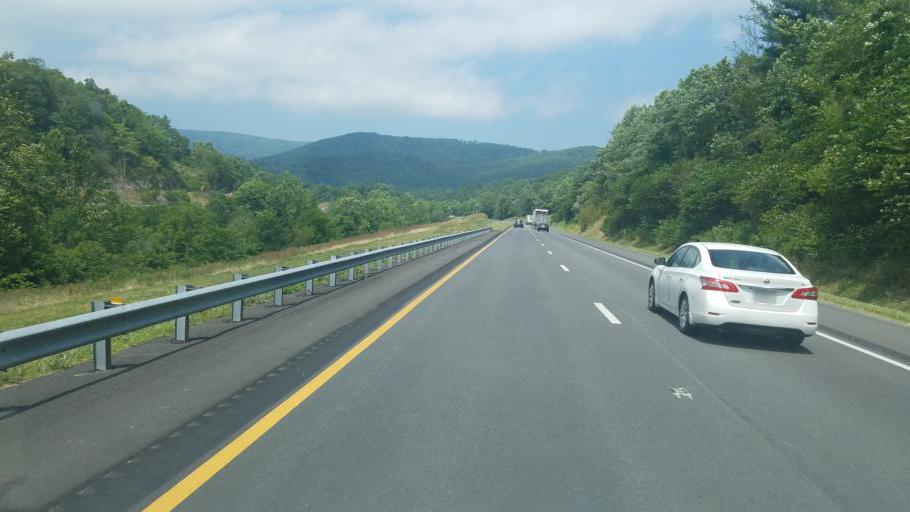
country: US
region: Virginia
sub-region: Bland County
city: Bland
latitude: 37.2309
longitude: -81.0951
